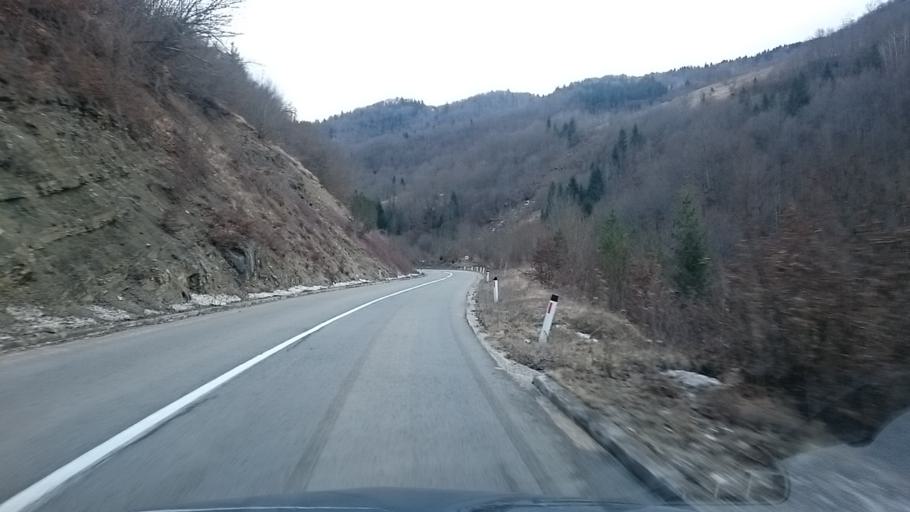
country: BA
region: Republika Srpska
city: Skender Vakuf
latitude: 44.4389
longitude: 17.3966
